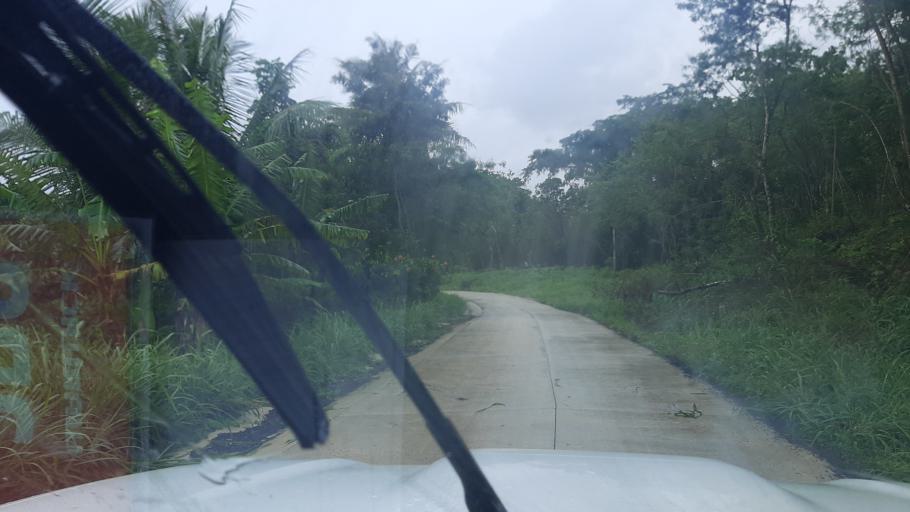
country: VU
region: Shefa
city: Port-Vila
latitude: -17.6381
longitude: 168.2118
